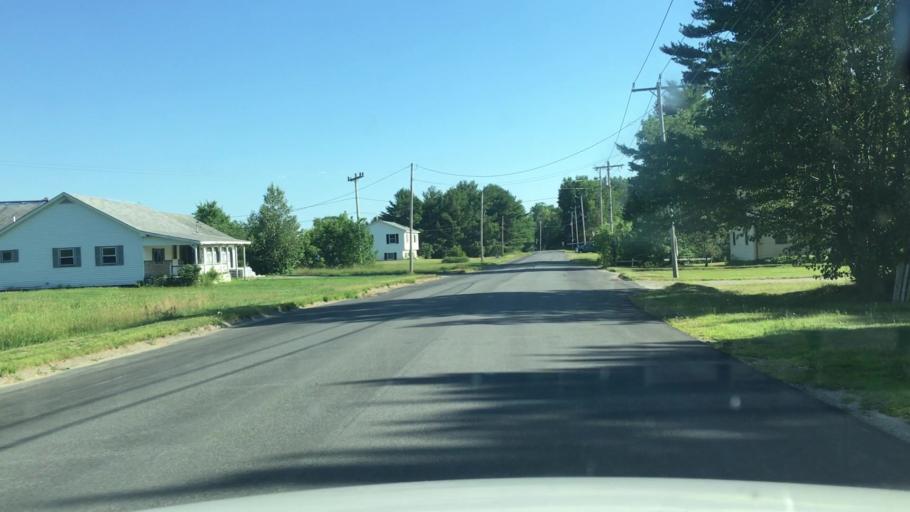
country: US
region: Maine
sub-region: Penobscot County
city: Howland
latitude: 45.2341
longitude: -68.6490
